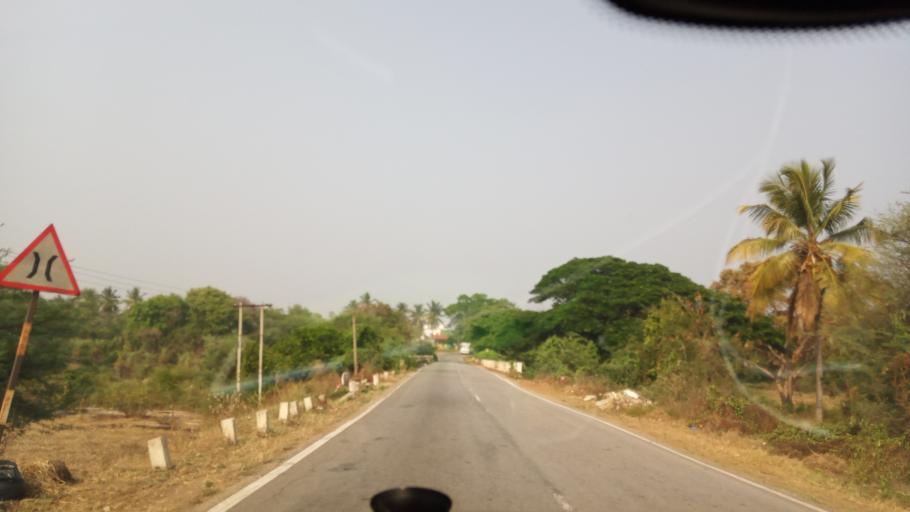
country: IN
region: Karnataka
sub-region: Mandya
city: Belluru
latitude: 12.9615
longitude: 76.7621
